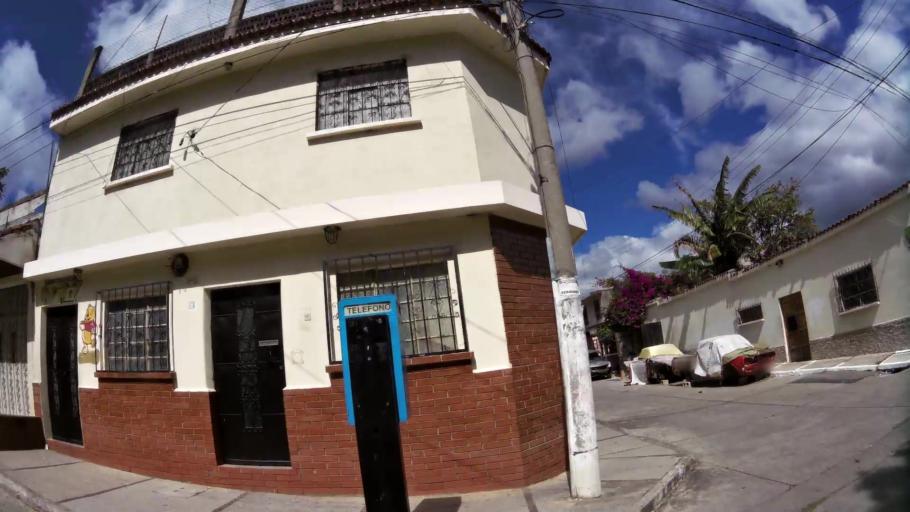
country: GT
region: Guatemala
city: Petapa
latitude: 14.5497
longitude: -90.5414
